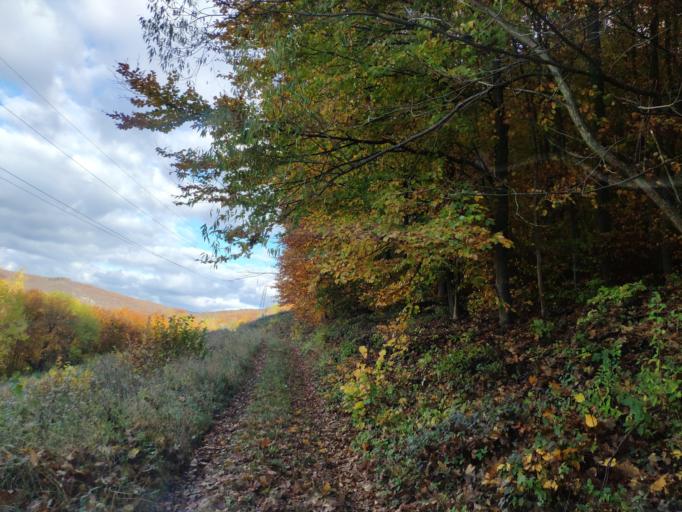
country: SK
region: Presovsky
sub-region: Okres Presov
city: Presov
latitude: 48.8517
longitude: 21.1814
